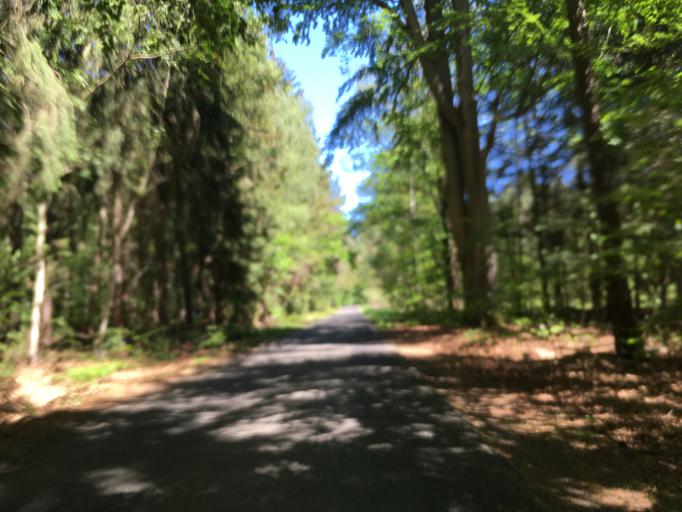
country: DE
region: Brandenburg
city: Zehdenick
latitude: 53.0045
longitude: 13.4478
